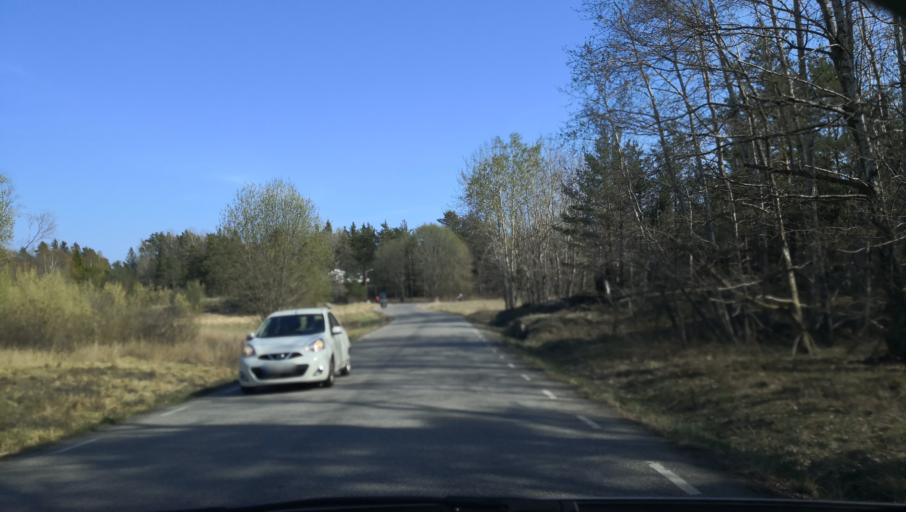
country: SE
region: Stockholm
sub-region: Varmdo Kommun
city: Holo
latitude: 59.3029
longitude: 18.6412
